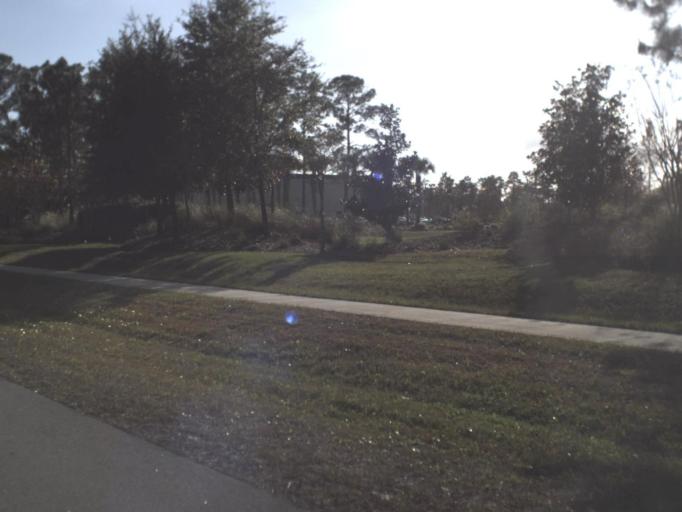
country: US
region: Florida
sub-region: Volusia County
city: Holly Hill
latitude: 29.2096
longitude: -81.0895
